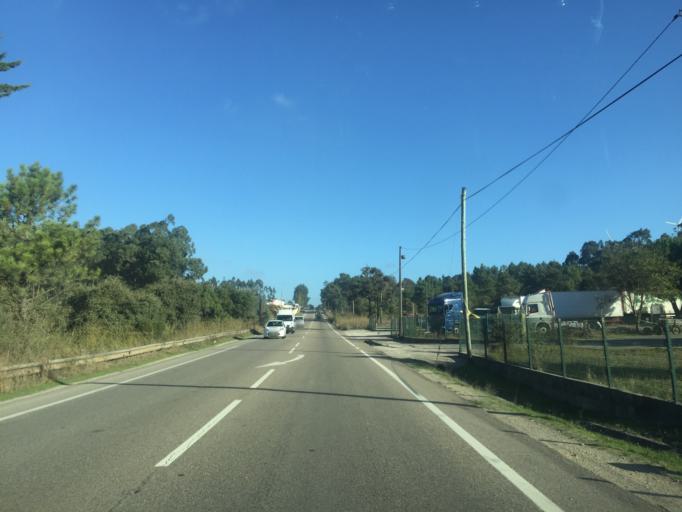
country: PT
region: Santarem
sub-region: Rio Maior
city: Rio Maior
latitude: 39.3769
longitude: -8.9627
